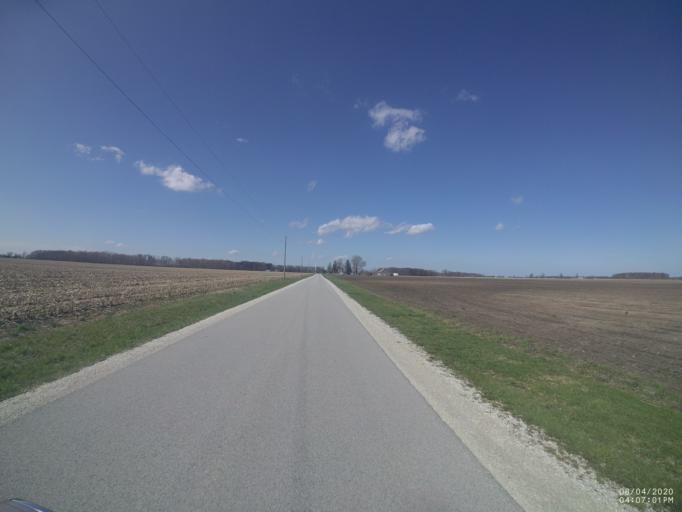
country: US
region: Ohio
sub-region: Sandusky County
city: Ballville
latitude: 41.2687
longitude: -83.2158
